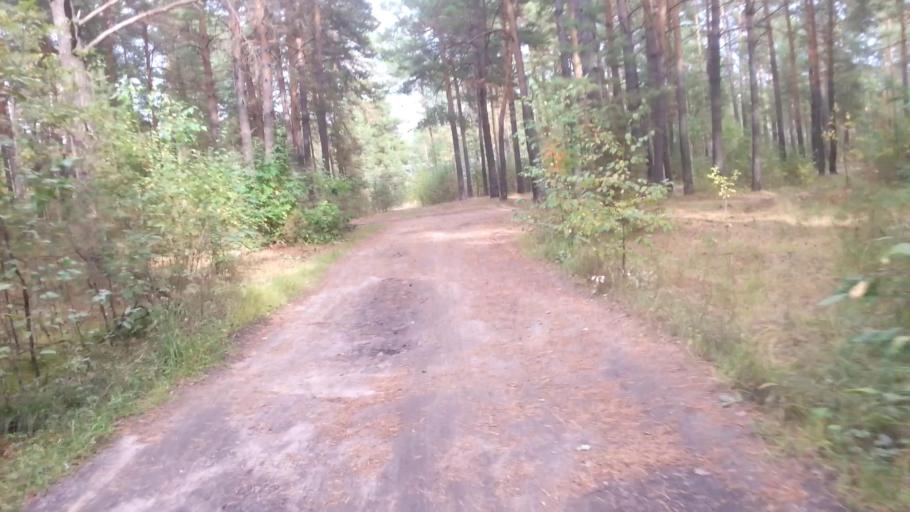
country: RU
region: Altai Krai
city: Yuzhnyy
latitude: 53.3109
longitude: 83.6977
